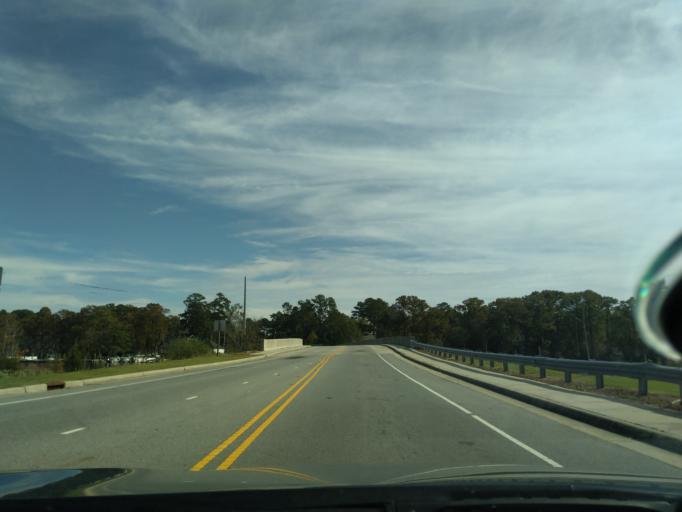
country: US
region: North Carolina
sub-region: Beaufort County
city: Washington
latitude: 35.5364
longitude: -77.0401
